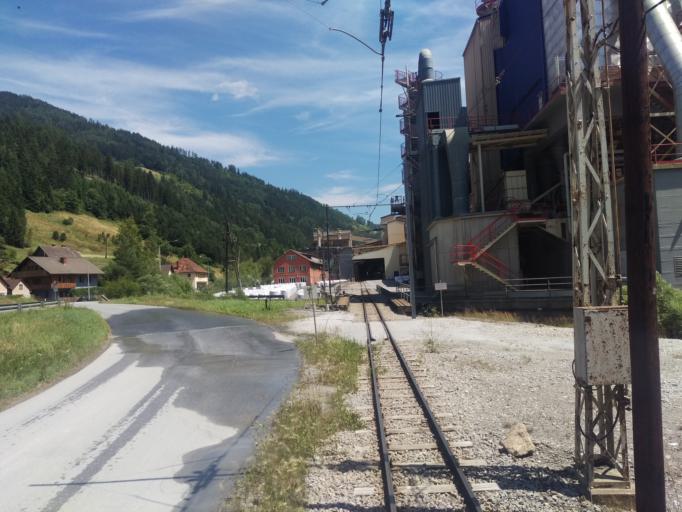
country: AT
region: Styria
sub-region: Politischer Bezirk Bruck-Muerzzuschlag
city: Allerheiligen im Muerztal
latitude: 47.3896
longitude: 15.4353
